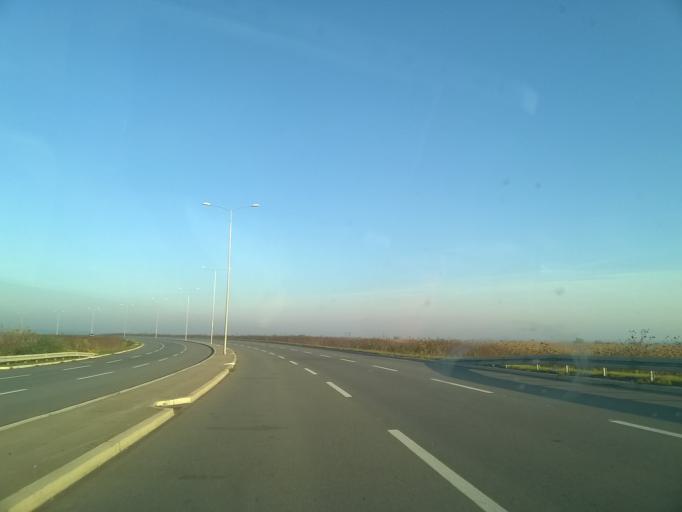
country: RS
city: Ovca
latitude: 44.9099
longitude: 20.5111
